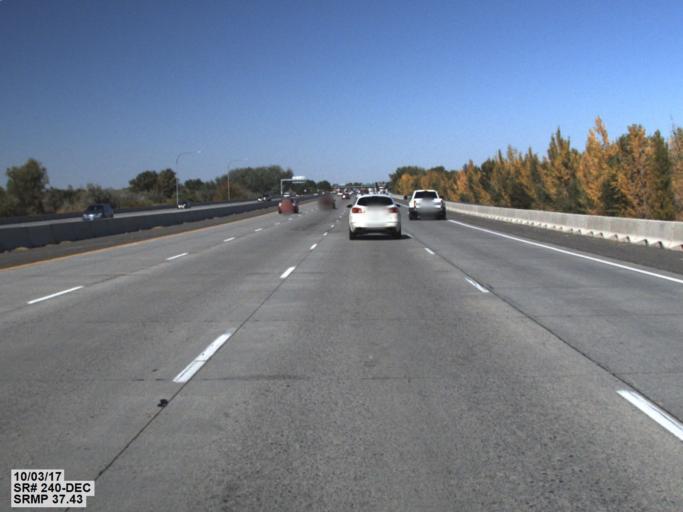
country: US
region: Washington
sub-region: Benton County
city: Richland
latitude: 46.2427
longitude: -119.2473
